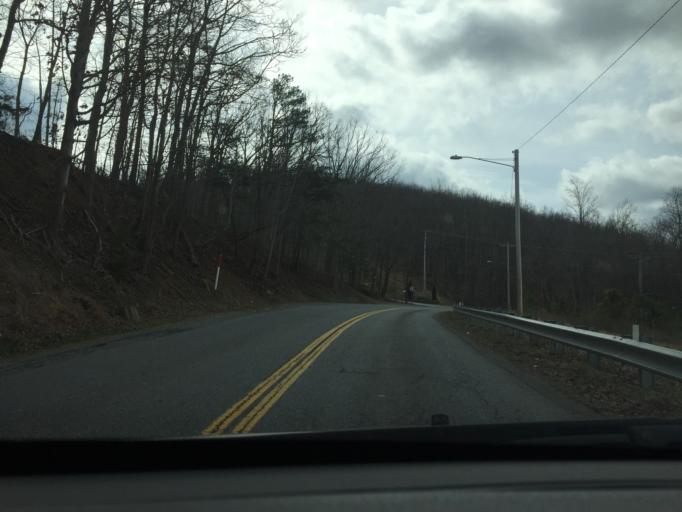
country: US
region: Virginia
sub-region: City of Lynchburg
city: West Lynchburg
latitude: 37.3527
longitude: -79.1691
